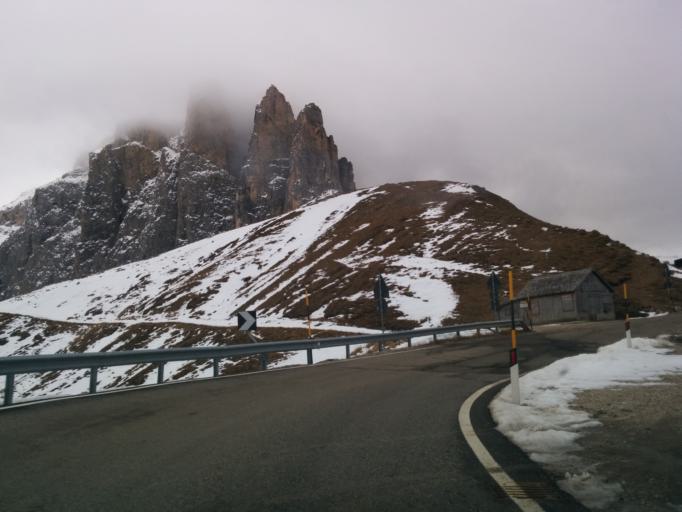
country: IT
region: Trentino-Alto Adige
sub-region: Provincia di Trento
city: Canazei
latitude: 46.5087
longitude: 11.7661
